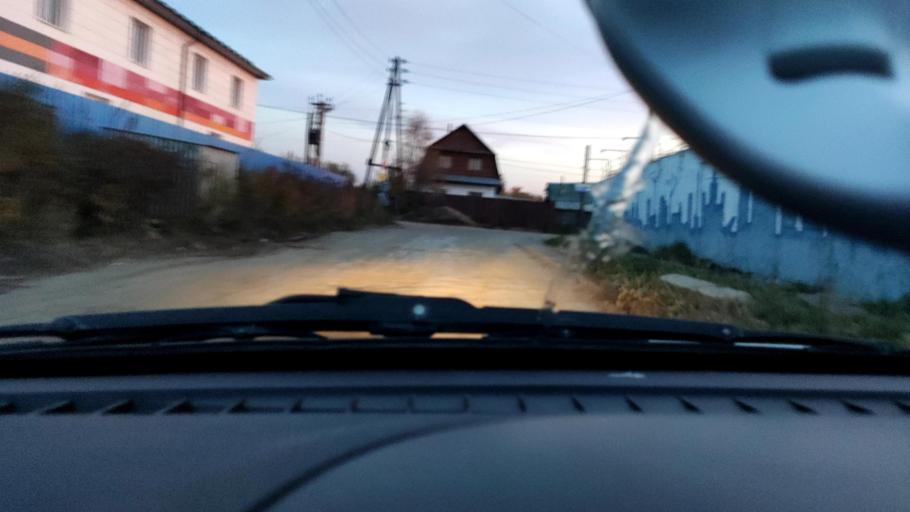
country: RU
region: Perm
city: Kondratovo
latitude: 58.0071
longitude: 56.0975
